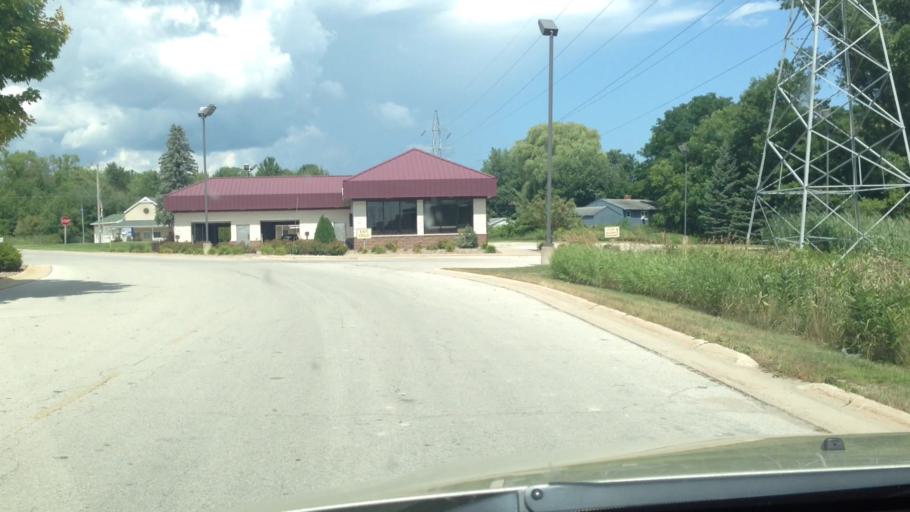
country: US
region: Wisconsin
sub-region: Brown County
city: Suamico
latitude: 44.6347
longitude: -88.0434
